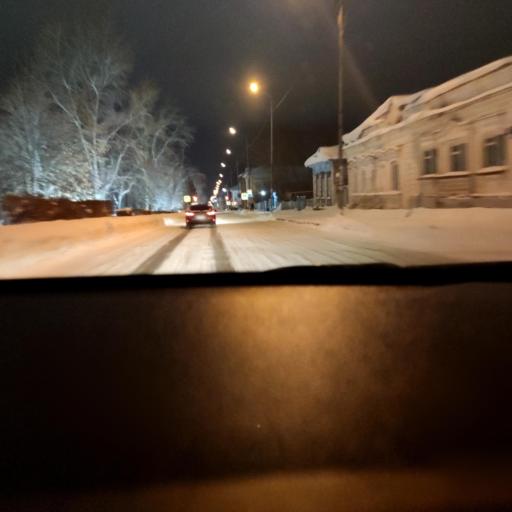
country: RU
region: Tatarstan
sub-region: Chistopol'skiy Rayon
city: Chistopol'
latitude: 55.3663
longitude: 50.6438
